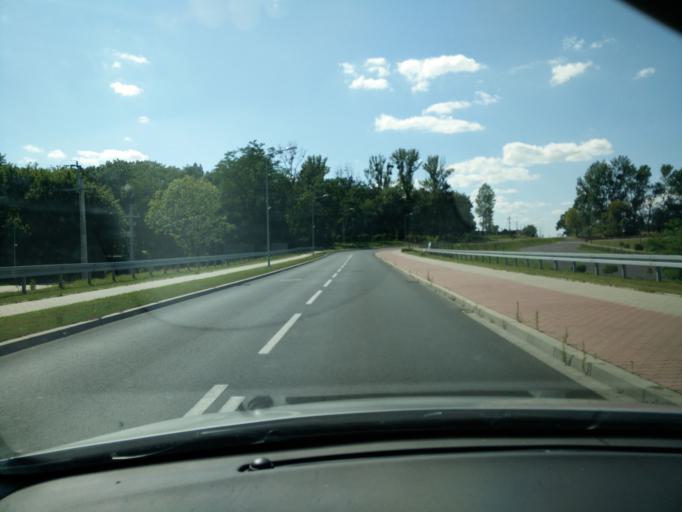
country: PL
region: Greater Poland Voivodeship
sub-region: Powiat sredzki
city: Sroda Wielkopolska
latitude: 52.2345
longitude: 17.2917
